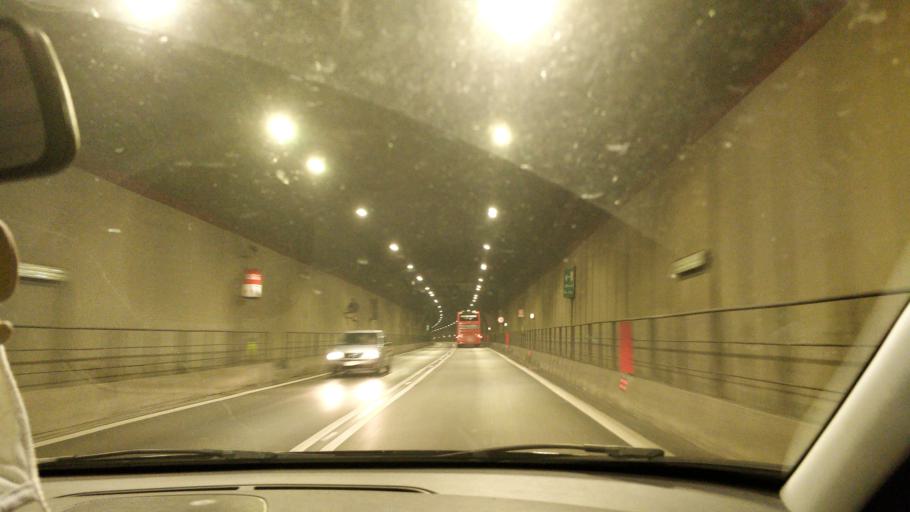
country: IT
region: Abruzzo
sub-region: Provincia di Chieti
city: Francavilla al Mare
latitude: 42.4100
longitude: 14.2946
